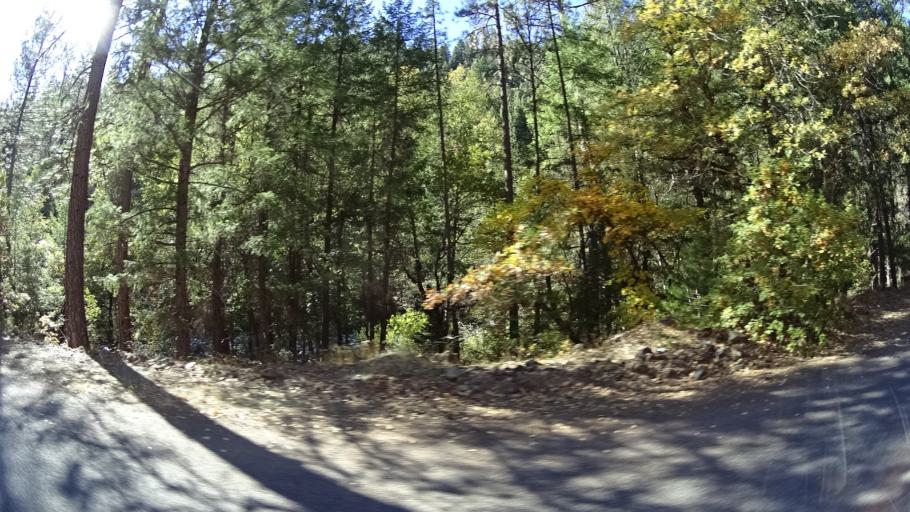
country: US
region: California
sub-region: Trinity County
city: Weaverville
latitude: 41.1409
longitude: -123.1002
